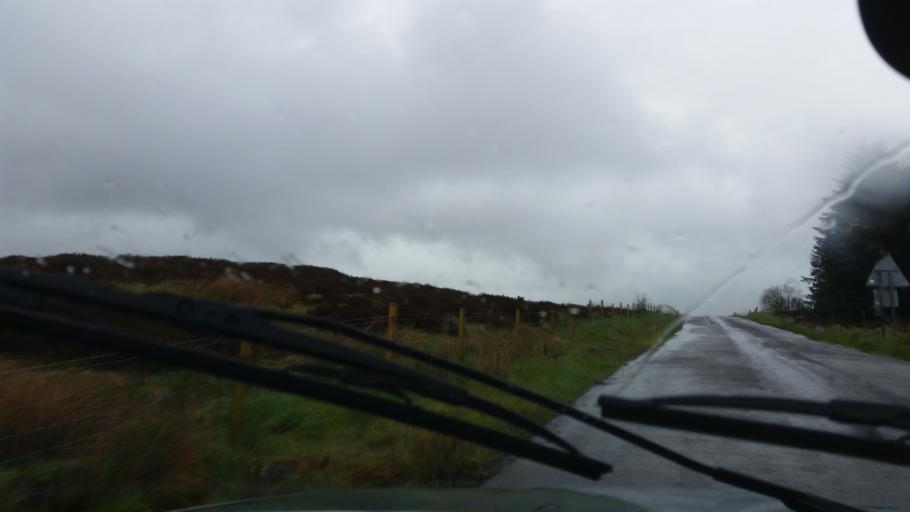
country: GB
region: Northern Ireland
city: Fivemiletown
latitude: 54.4345
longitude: -7.3276
